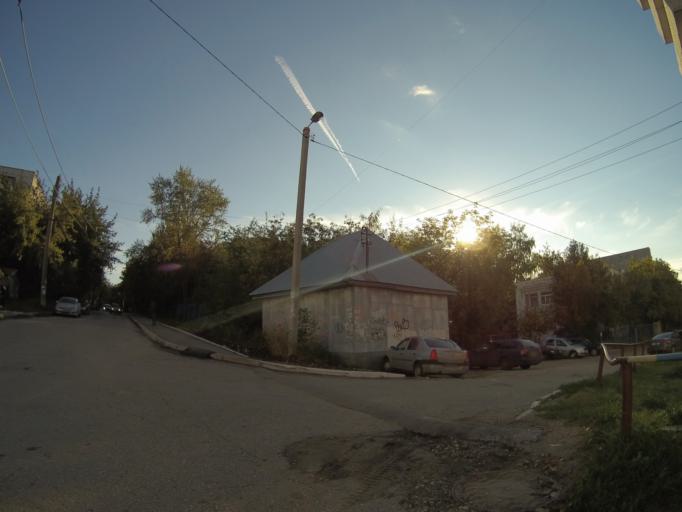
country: RU
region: Vladimir
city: Vladimir
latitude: 56.1538
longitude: 40.3735
